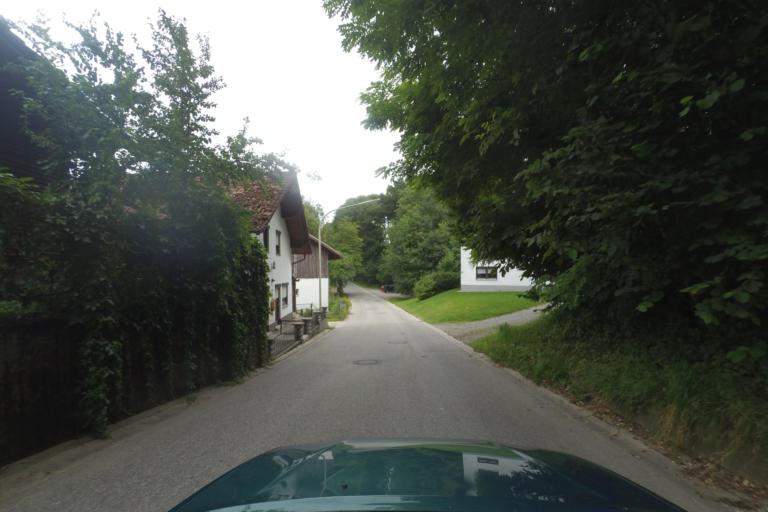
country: DE
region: Bavaria
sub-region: Lower Bavaria
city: Pilsting
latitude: 48.6630
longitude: 12.6482
